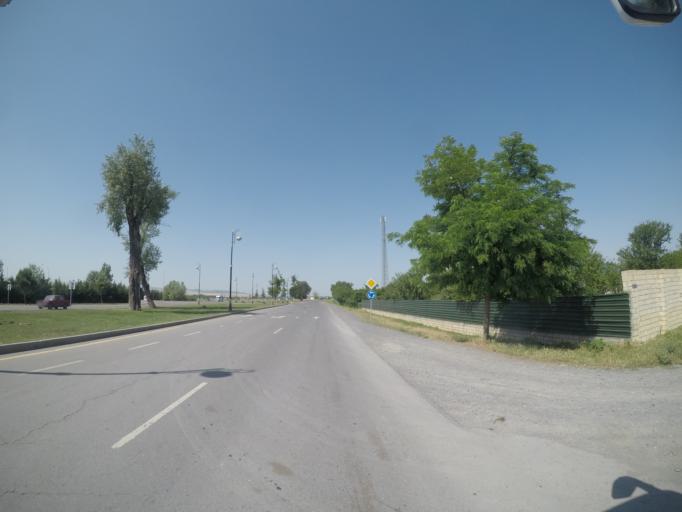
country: AZ
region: Goeycay
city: Geoktschai
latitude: 40.8310
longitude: 47.7093
